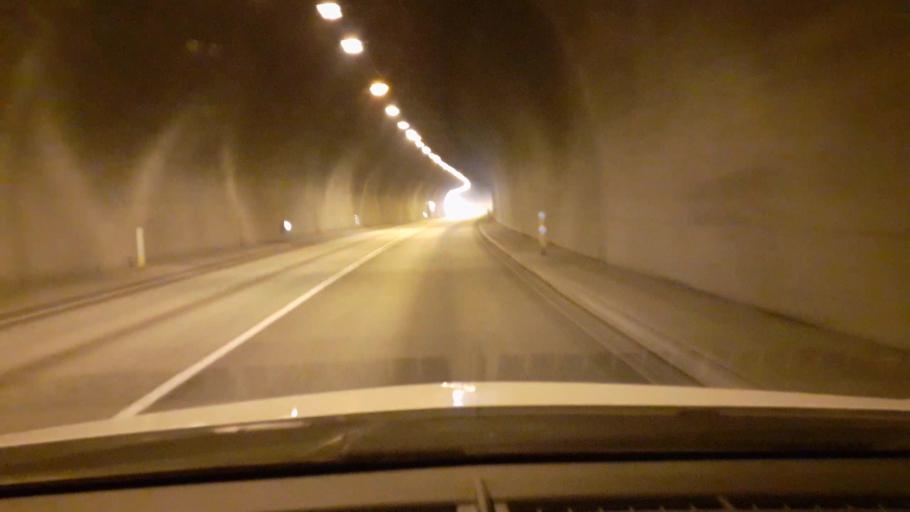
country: IS
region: Capital Region
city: Reykjavik
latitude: 64.2834
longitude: -21.8425
